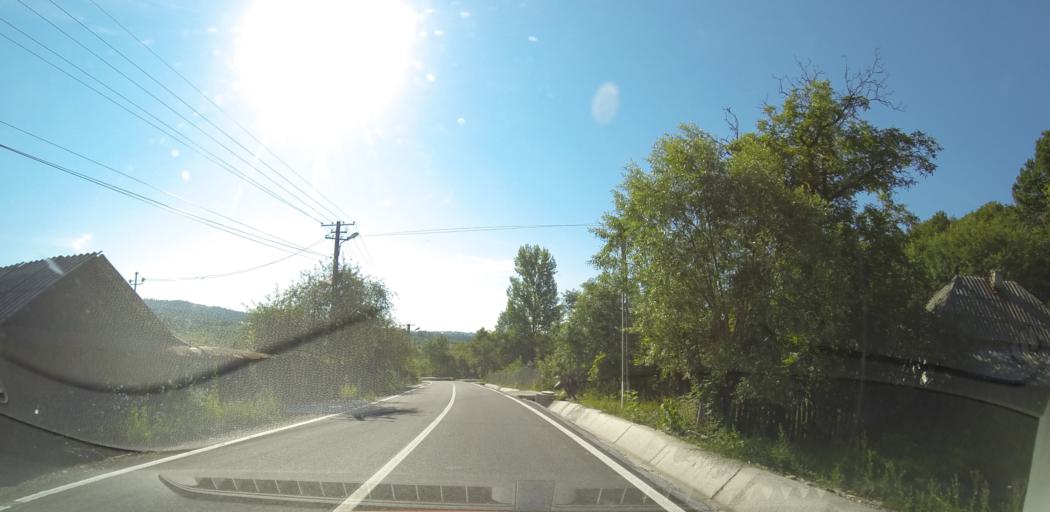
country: RO
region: Gorj
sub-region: Comuna Polovragi
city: Polovragi
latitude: 45.1729
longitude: 23.8636
